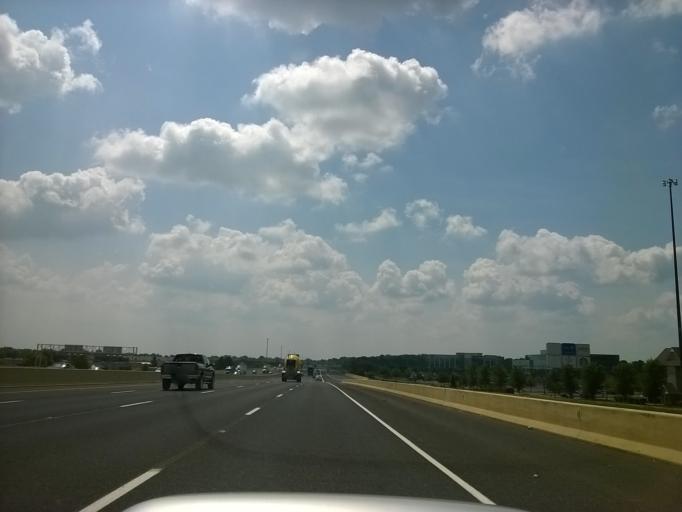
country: US
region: Indiana
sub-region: Boone County
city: Zionsville
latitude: 39.8805
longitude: -86.2692
